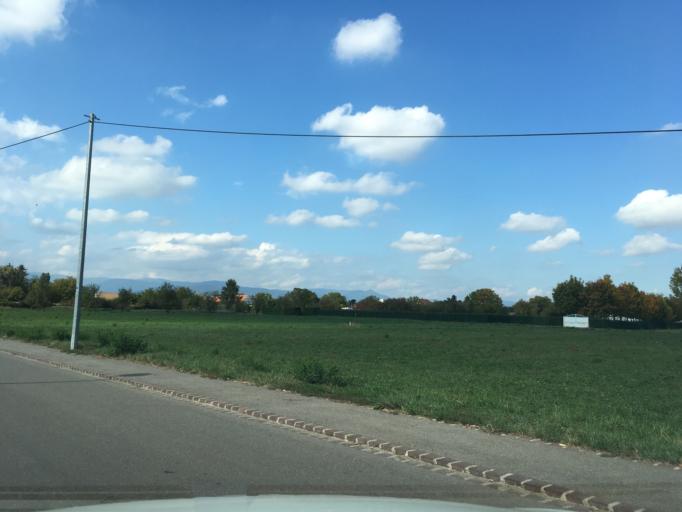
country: FR
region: Alsace
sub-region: Departement du Haut-Rhin
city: Colmar
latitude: 48.0634
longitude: 7.3737
